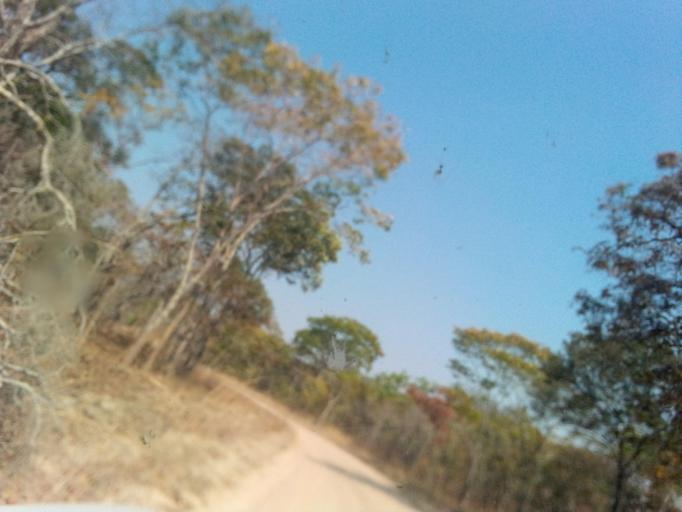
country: ZM
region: Northern
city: Mpika
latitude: -12.2248
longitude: 30.8964
